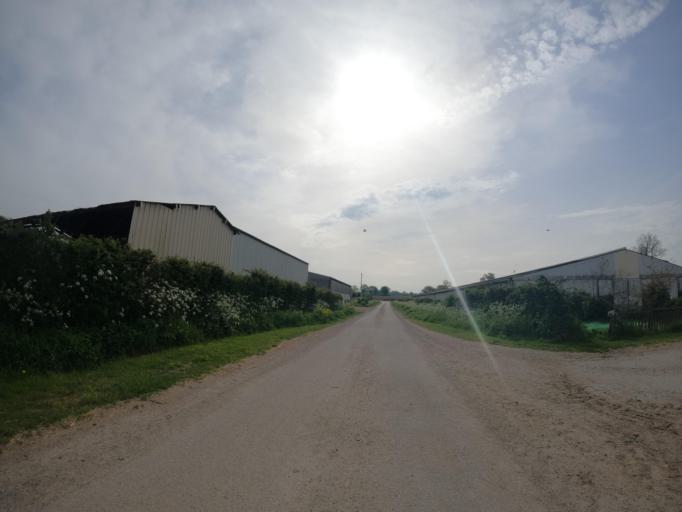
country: FR
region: Poitou-Charentes
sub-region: Departement des Deux-Sevres
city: Moncoutant
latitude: 46.6969
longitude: -0.5536
